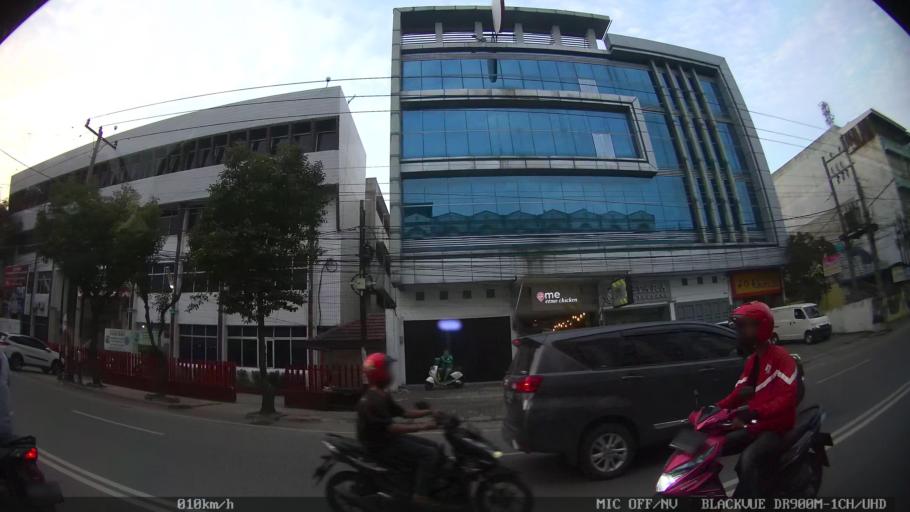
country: ID
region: North Sumatra
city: Medan
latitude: 3.5878
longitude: 98.6957
